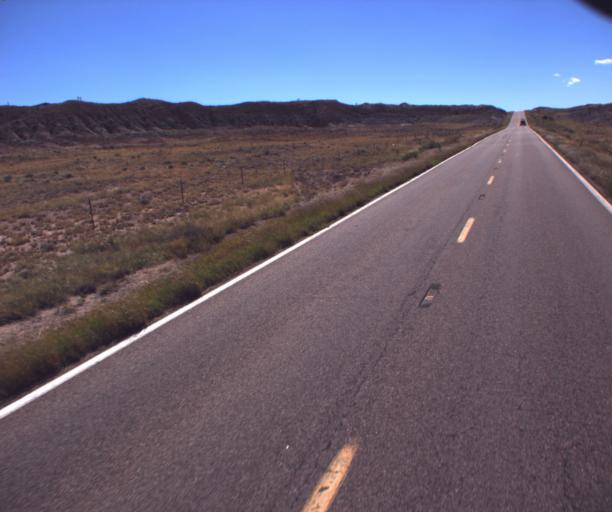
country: US
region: Arizona
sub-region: Apache County
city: Saint Johns
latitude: 34.6626
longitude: -109.2926
